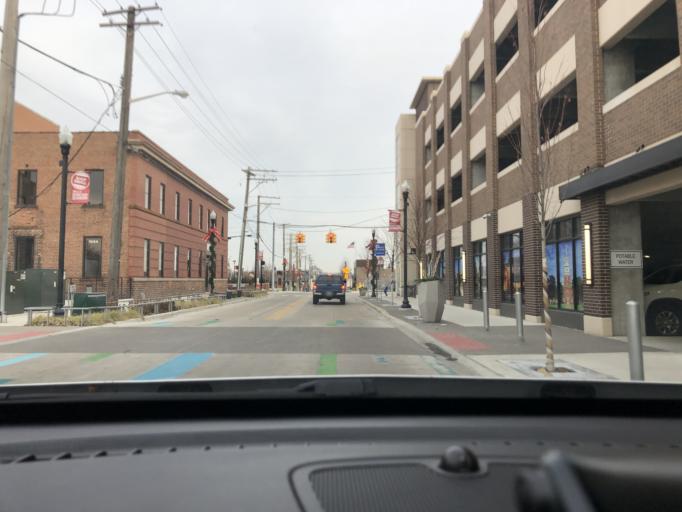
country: US
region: Michigan
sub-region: Wayne County
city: Dearborn Heights
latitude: 42.3054
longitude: -83.2445
